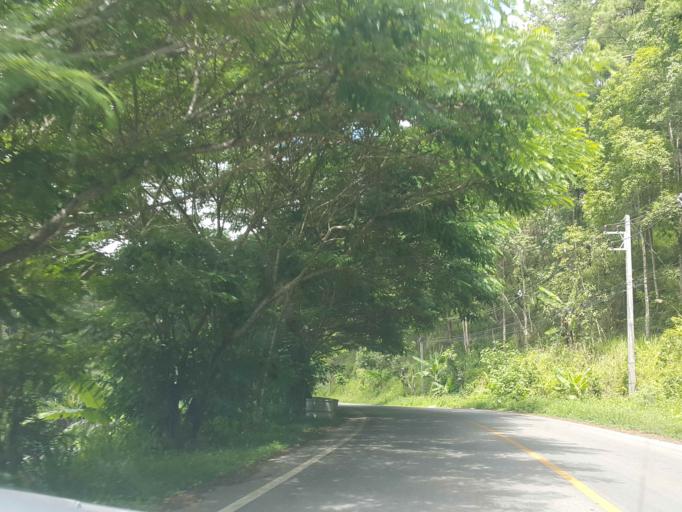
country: TH
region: Chiang Mai
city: Samoeng
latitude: 18.8768
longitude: 98.7903
